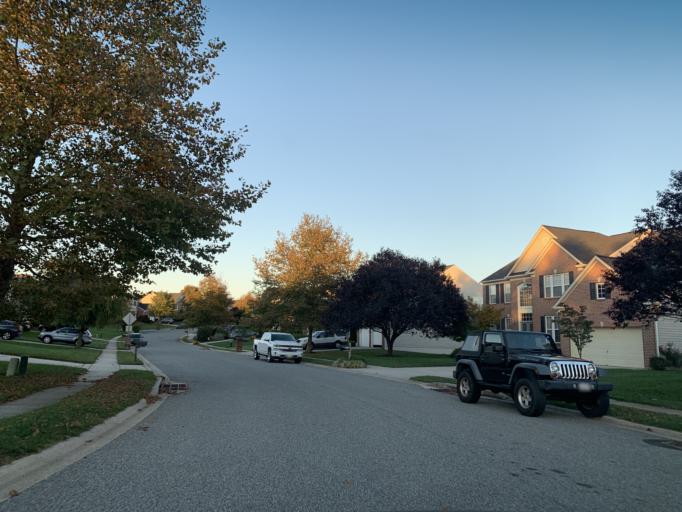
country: US
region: Maryland
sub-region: Harford County
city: Bel Air South
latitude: 39.5278
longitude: -76.2998
